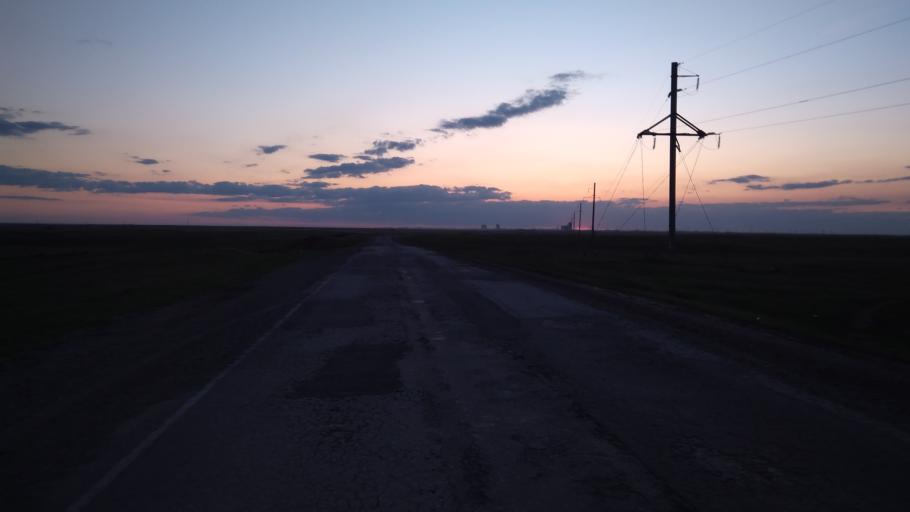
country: RU
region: Chelyabinsk
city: Troitsk
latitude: 54.0866
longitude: 61.6625
